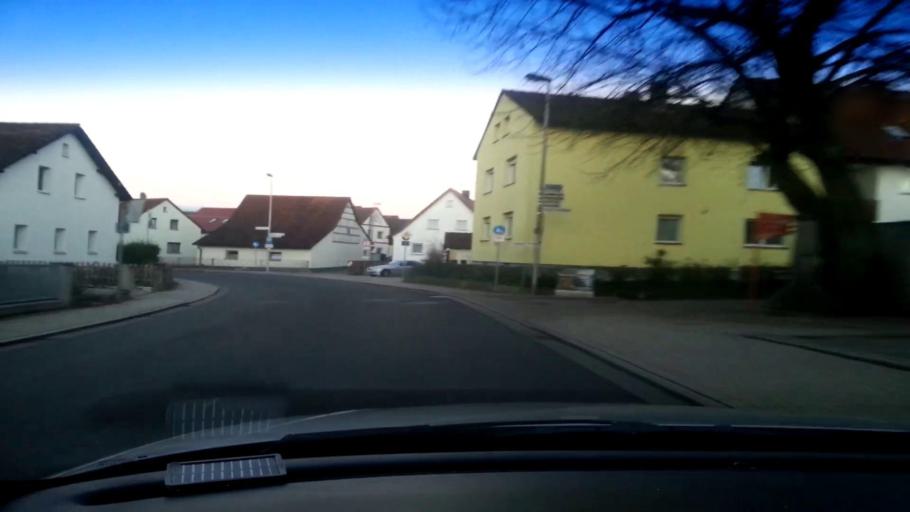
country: DE
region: Bavaria
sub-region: Upper Franconia
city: Litzendorf
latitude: 49.9110
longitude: 10.9896
